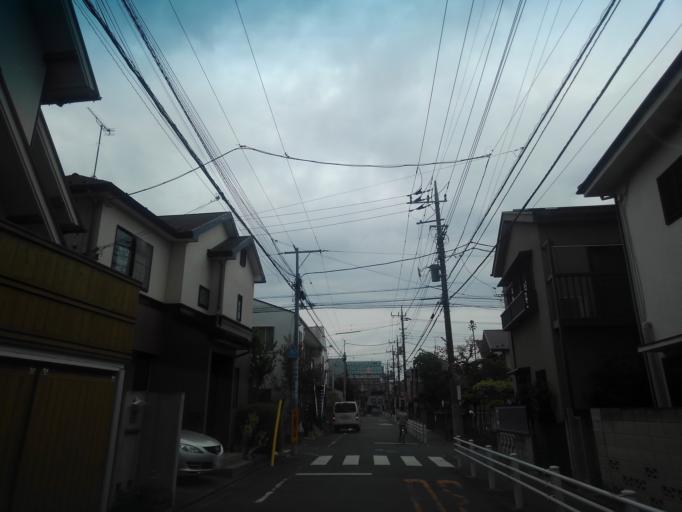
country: JP
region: Tokyo
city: Musashino
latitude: 35.7014
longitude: 139.5866
